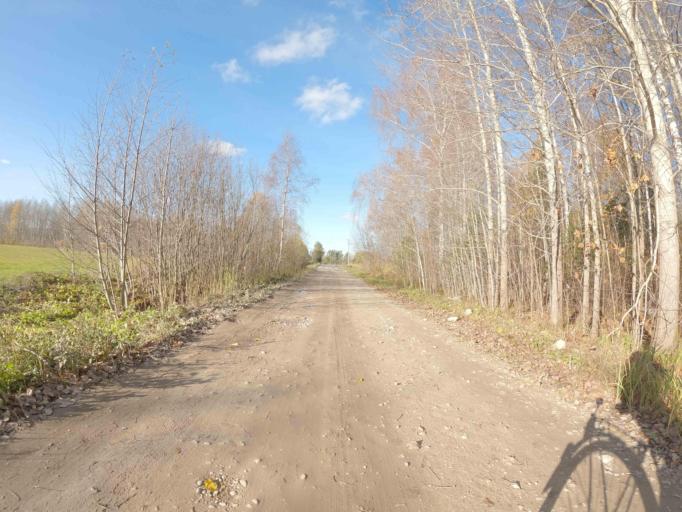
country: EE
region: Raplamaa
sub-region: Rapla vald
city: Rapla
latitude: 59.0094
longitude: 24.8026
